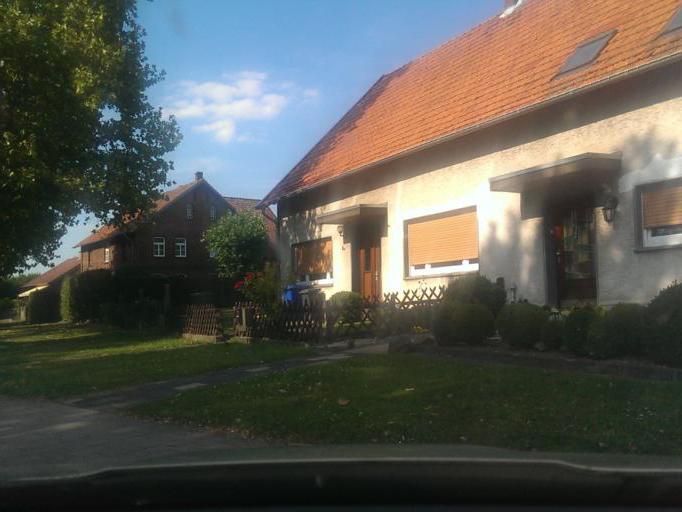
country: DE
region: North Rhine-Westphalia
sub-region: Regierungsbezirk Detmold
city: Salzkotten
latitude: 51.6746
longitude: 8.6076
